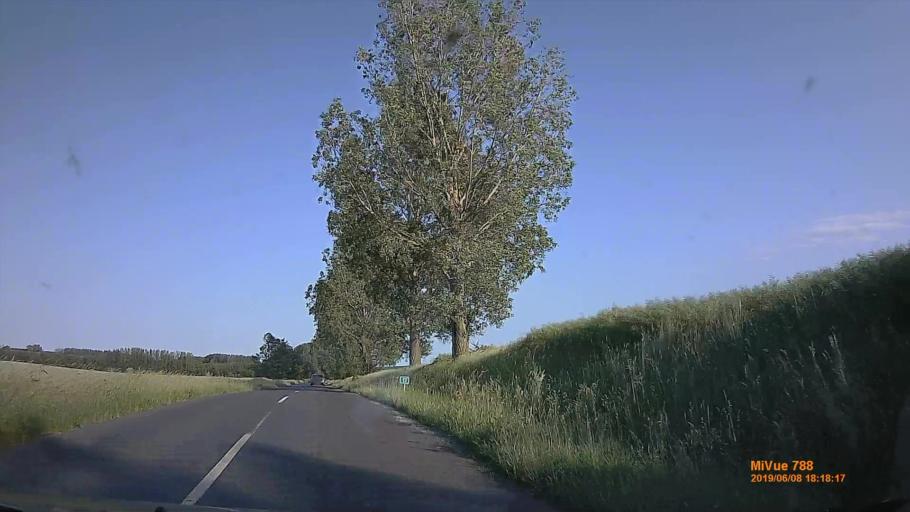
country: HU
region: Vas
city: Buk
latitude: 47.3751
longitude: 16.7263
